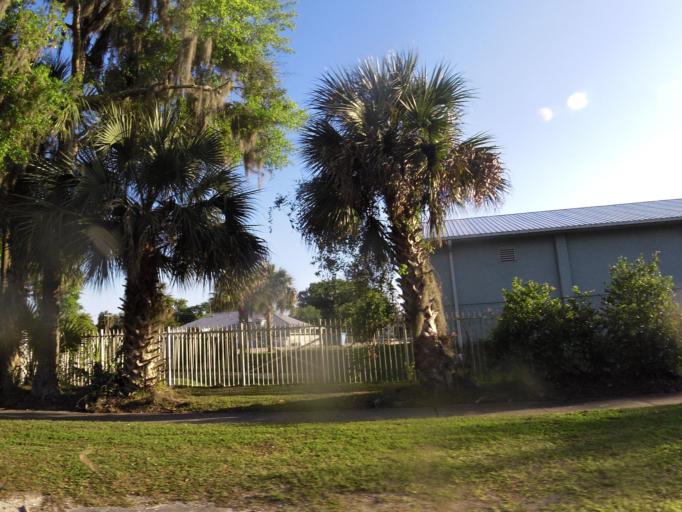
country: US
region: Florida
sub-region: Putnam County
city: Palatka
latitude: 29.6502
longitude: -81.6333
